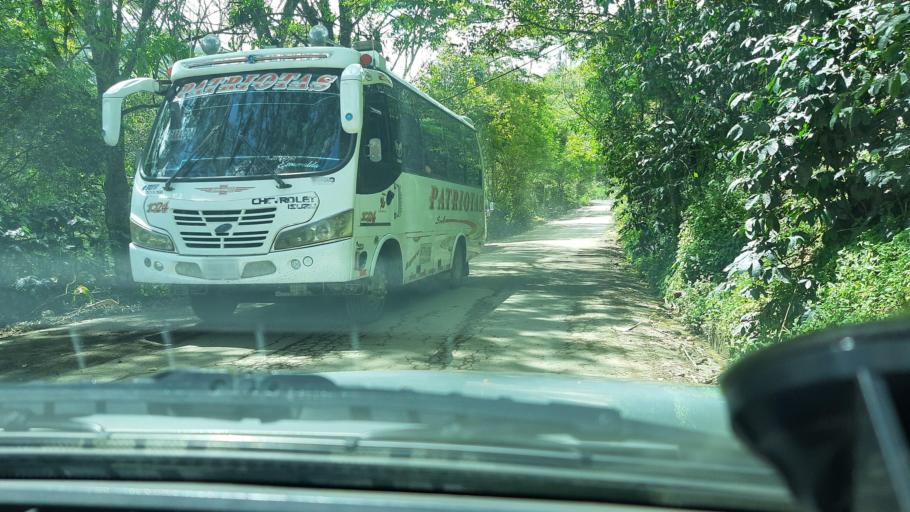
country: CO
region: Boyaca
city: Chinavita
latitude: 5.1793
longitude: -73.3828
